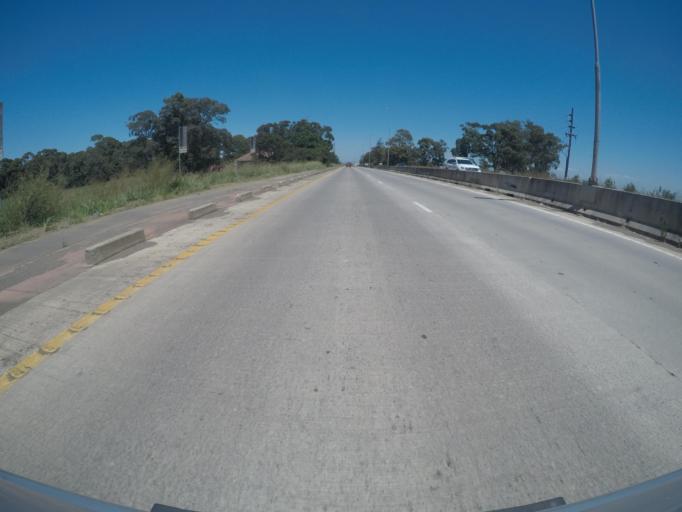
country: ZA
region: Eastern Cape
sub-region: Buffalo City Metropolitan Municipality
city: East London
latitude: -32.9377
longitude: 27.9821
